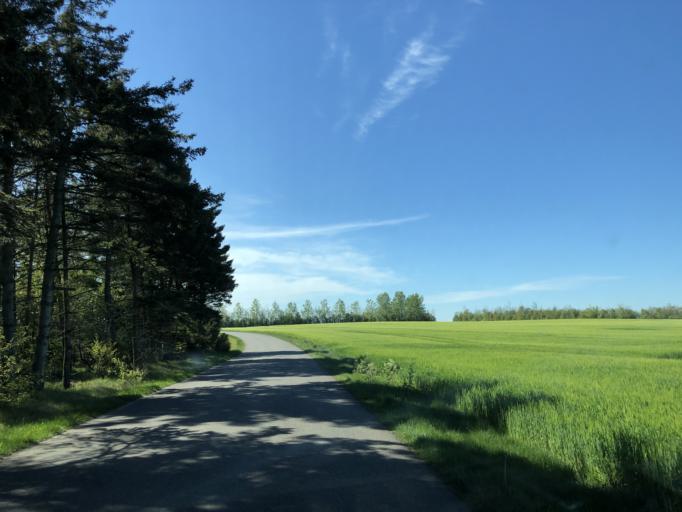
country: DK
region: Central Jutland
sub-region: Ringkobing-Skjern Kommune
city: Videbaek
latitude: 56.1987
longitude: 8.5121
